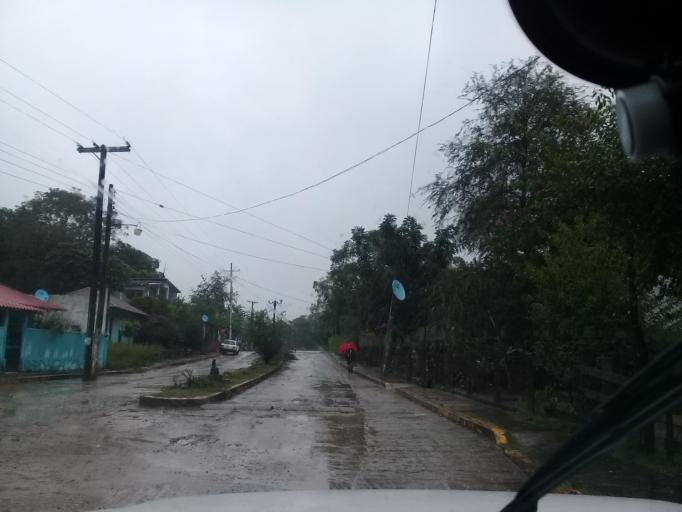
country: MX
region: Veracruz
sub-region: Chalma
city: San Pedro Coyutla
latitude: 21.2351
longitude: -98.4604
